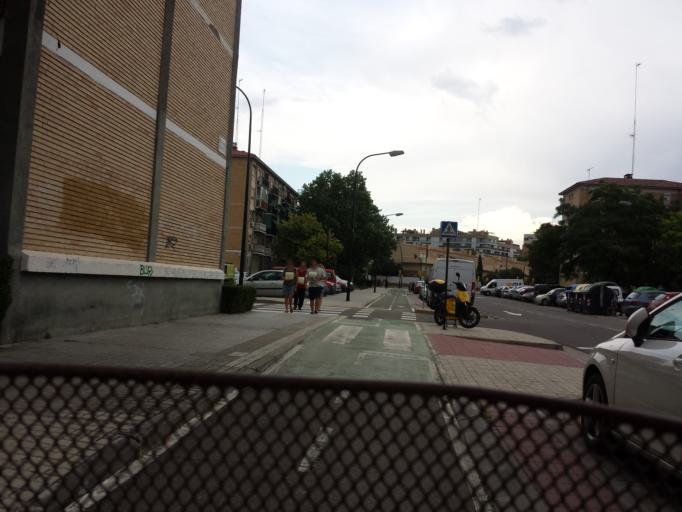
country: ES
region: Aragon
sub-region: Provincia de Zaragoza
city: Zaragoza
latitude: 41.6637
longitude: -0.8736
